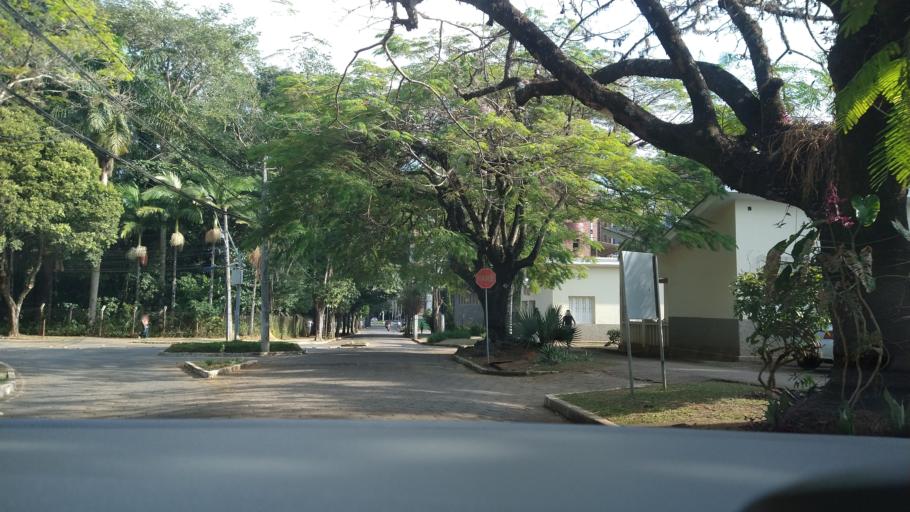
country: BR
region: Minas Gerais
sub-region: Vicosa
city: Vicosa
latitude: -20.7556
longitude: -42.8741
